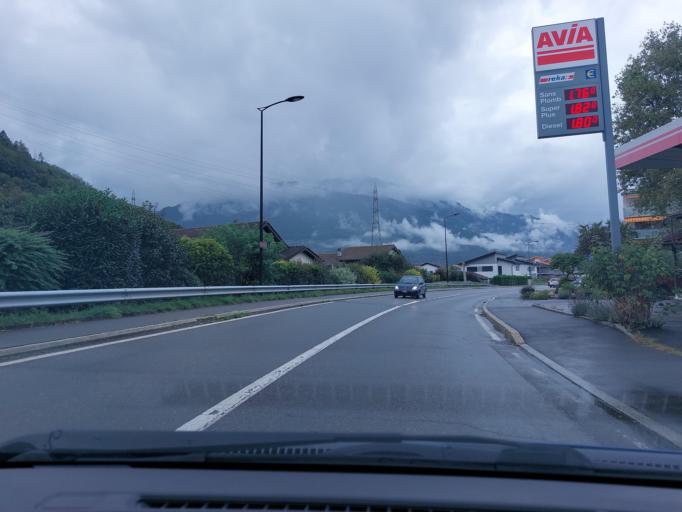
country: CH
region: Valais
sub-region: Monthey District
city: Monthey
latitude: 46.2435
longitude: 6.9844
